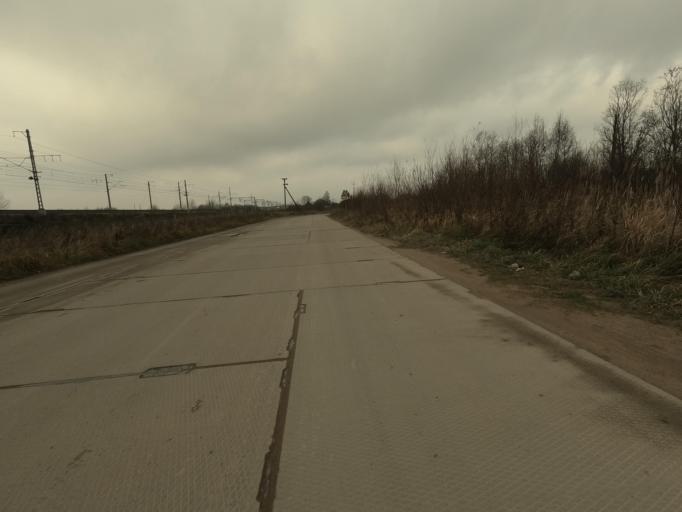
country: RU
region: Leningrad
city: Lyuban'
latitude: 59.4786
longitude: 31.2585
